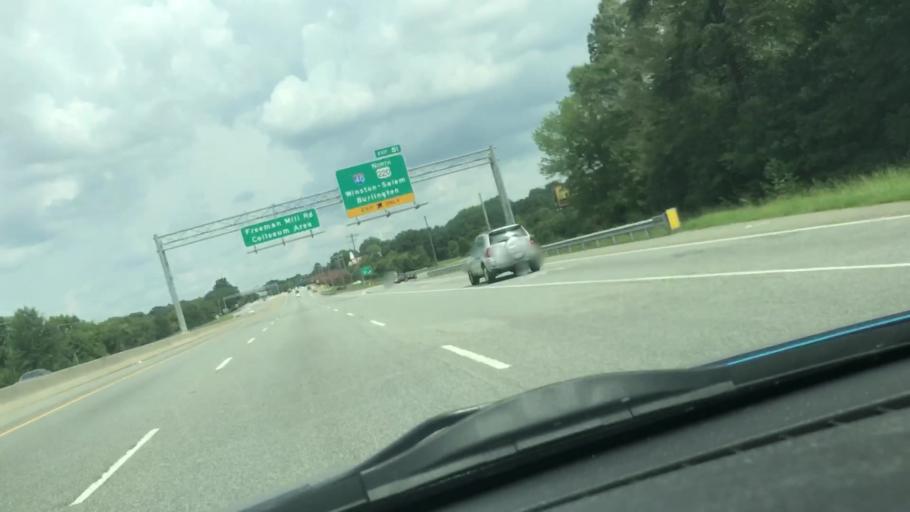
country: US
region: North Carolina
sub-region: Guilford County
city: Greensboro
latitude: 36.0311
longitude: -79.8220
